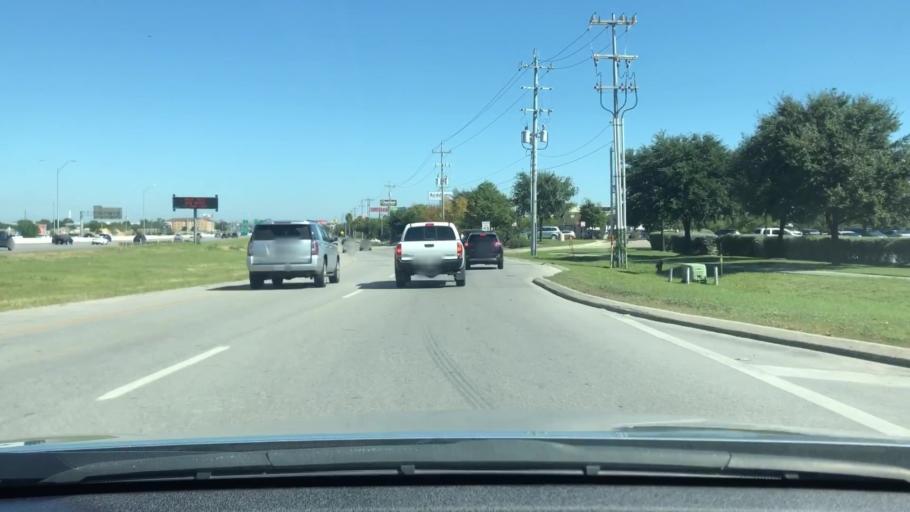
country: US
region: Texas
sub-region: Bexar County
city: Selma
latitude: 29.5777
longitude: -98.3198
